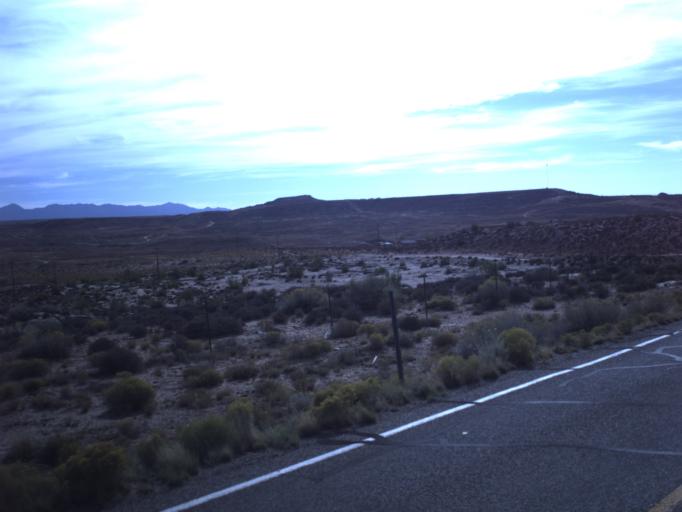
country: US
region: Utah
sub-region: San Juan County
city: Blanding
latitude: 37.3142
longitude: -109.3052
